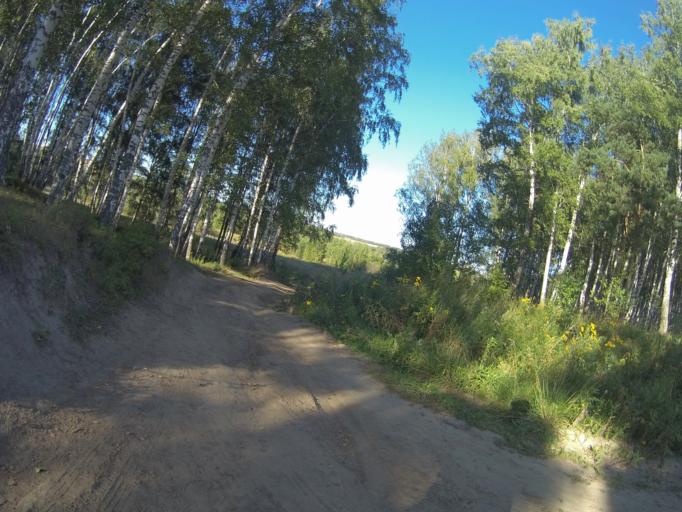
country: RU
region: Vladimir
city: Vladimir
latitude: 56.1917
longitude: 40.3780
